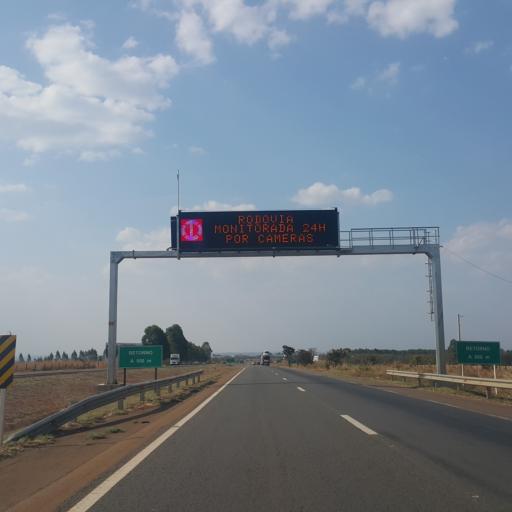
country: BR
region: Goias
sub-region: Abadiania
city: Abadiania
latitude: -16.2133
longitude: -48.7453
